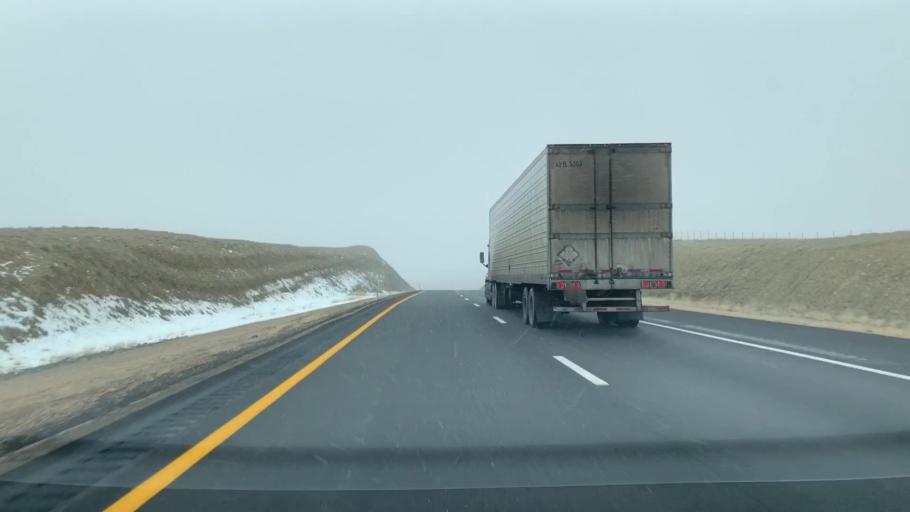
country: US
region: Utah
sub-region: Carbon County
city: East Carbon City
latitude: 38.9412
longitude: -110.3353
